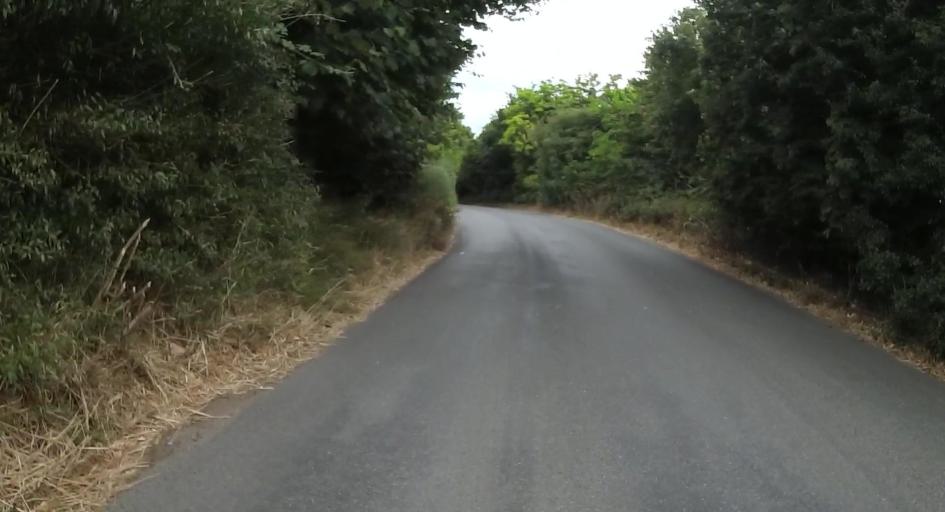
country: GB
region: England
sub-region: Dorset
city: Wareham
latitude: 50.6349
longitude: -2.0689
